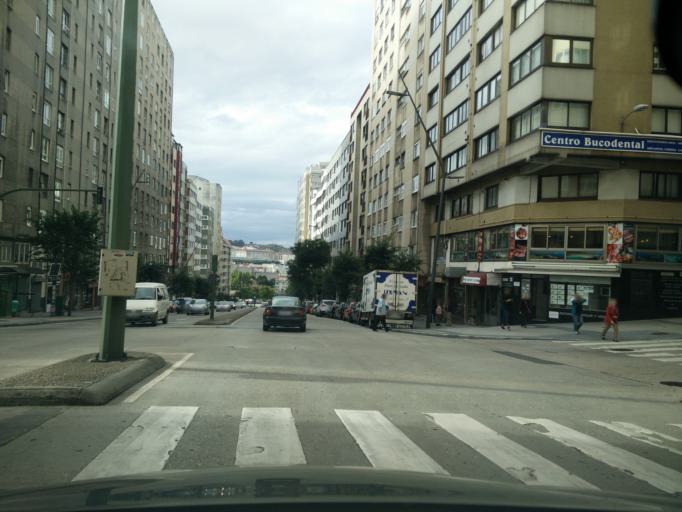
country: ES
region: Galicia
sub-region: Provincia da Coruna
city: A Coruna
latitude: 43.3632
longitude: -8.4229
